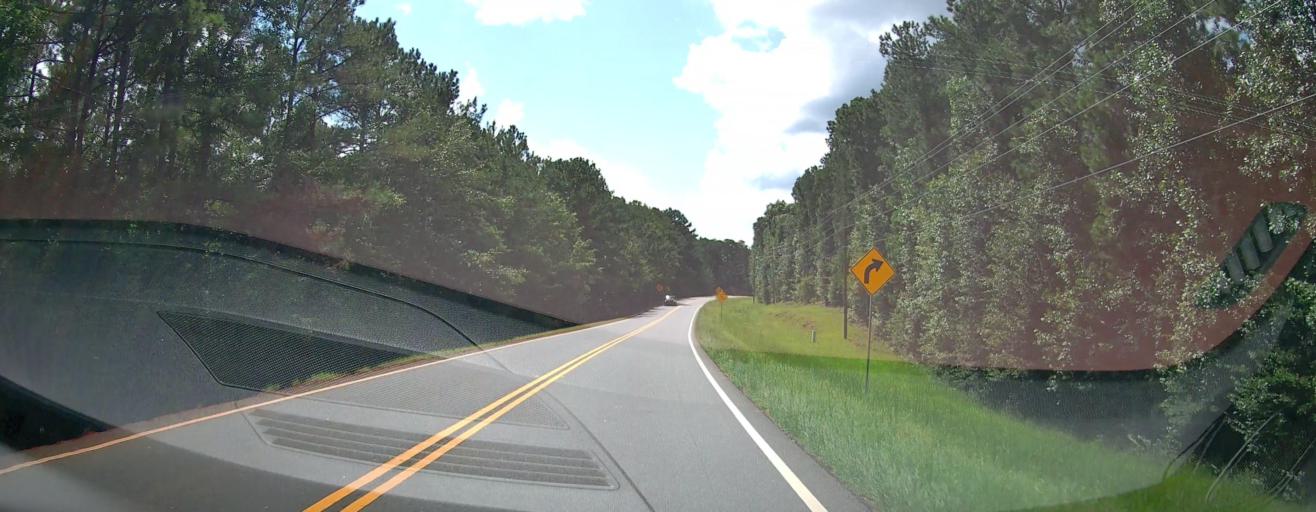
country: US
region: Georgia
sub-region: Monroe County
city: Forsyth
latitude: 32.8792
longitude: -83.9551
